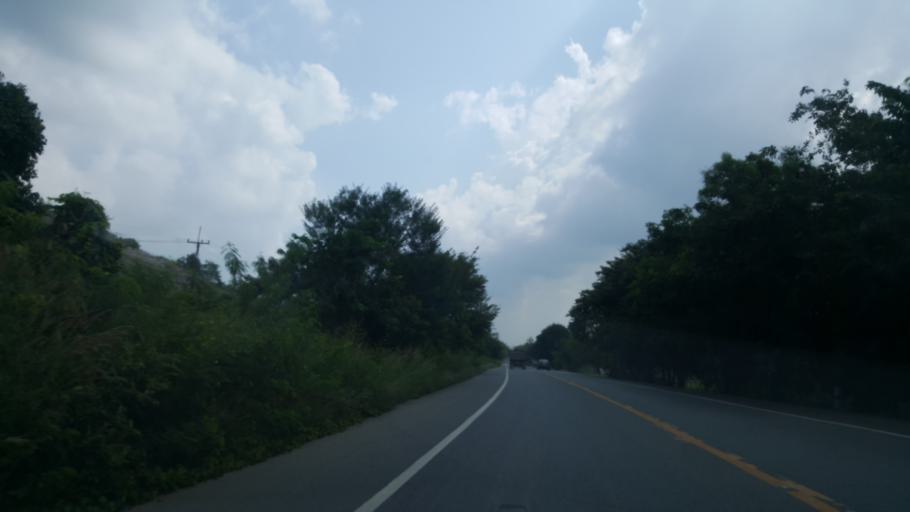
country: TH
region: Chon Buri
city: Sattahip
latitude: 12.7262
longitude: 100.9624
